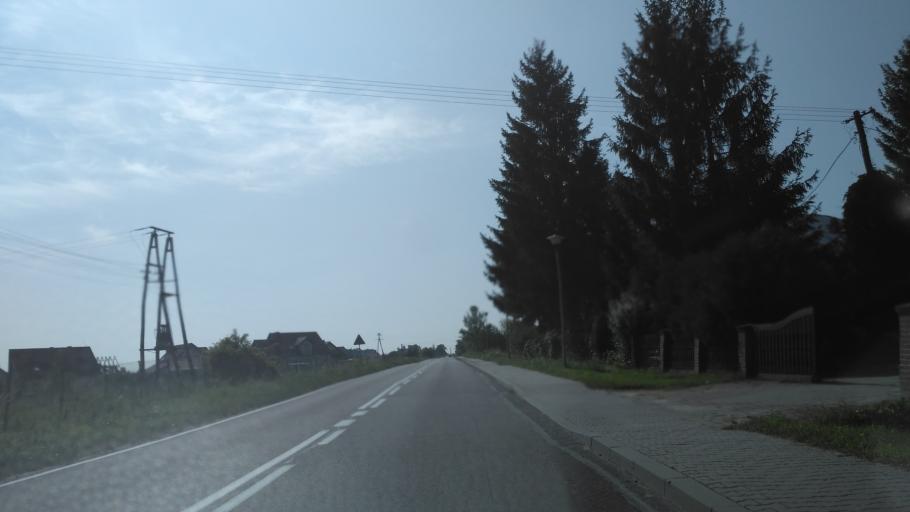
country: PL
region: Lublin Voivodeship
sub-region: Powiat chelmski
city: Rejowiec Fabryczny
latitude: 51.1893
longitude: 23.1639
